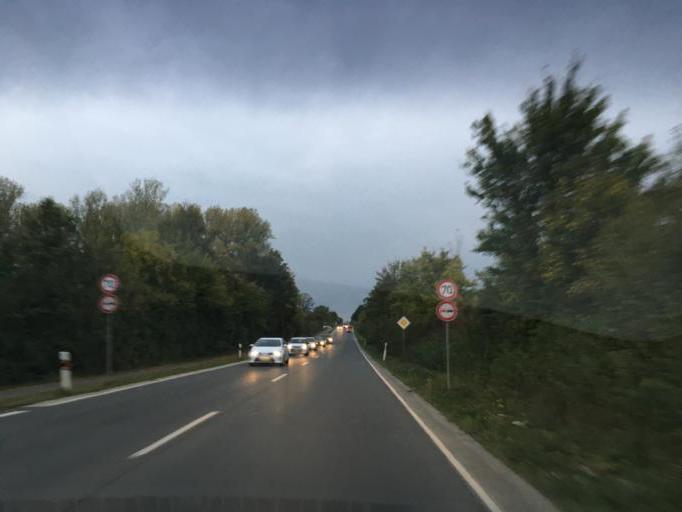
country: DE
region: North Rhine-Westphalia
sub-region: Regierungsbezirk Koln
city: Kreuzau
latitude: 50.7578
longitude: 6.5303
